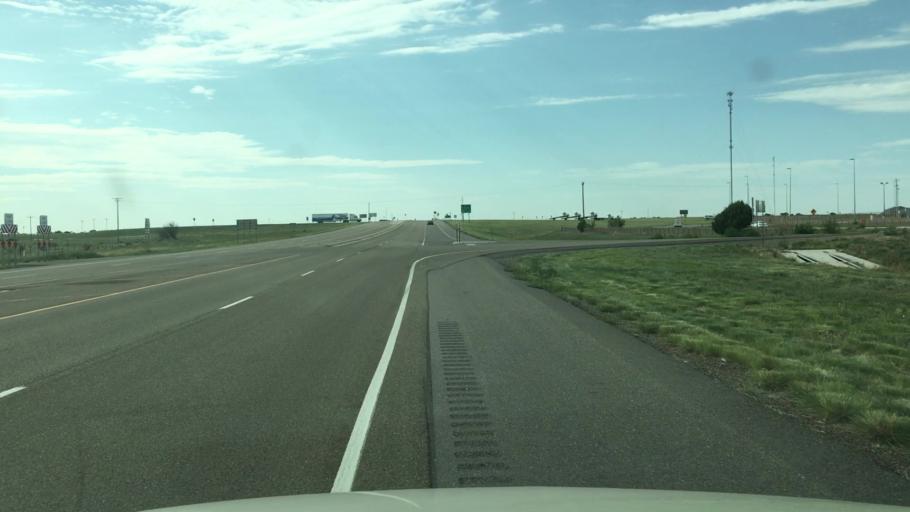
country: US
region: New Mexico
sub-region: Torrance County
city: Moriarty
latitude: 35.0127
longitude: -105.6667
